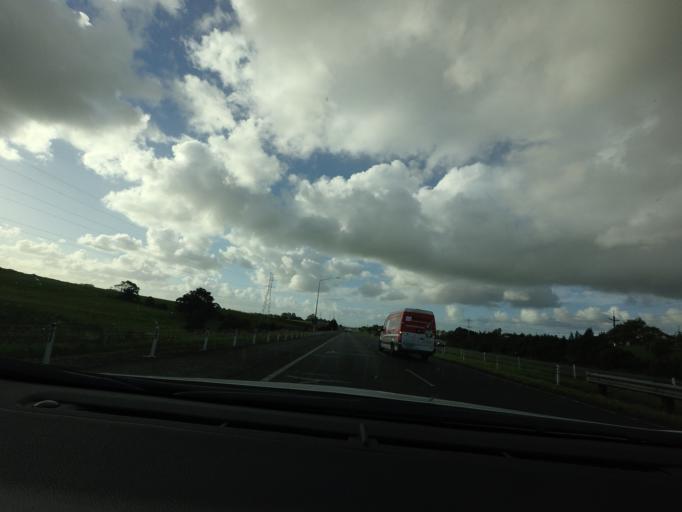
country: NZ
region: Auckland
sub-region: Auckland
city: Pukekohe East
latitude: -37.1533
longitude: 174.9755
